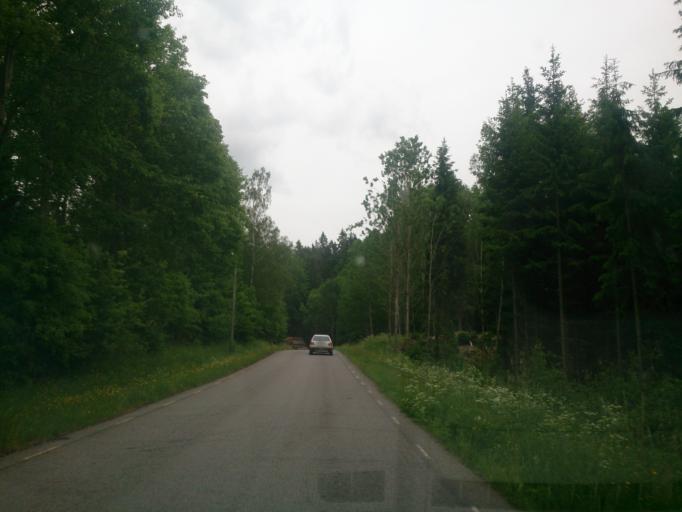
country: SE
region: OEstergoetland
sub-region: Soderkopings Kommun
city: Soederkoeping
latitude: 58.3156
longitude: 16.3206
